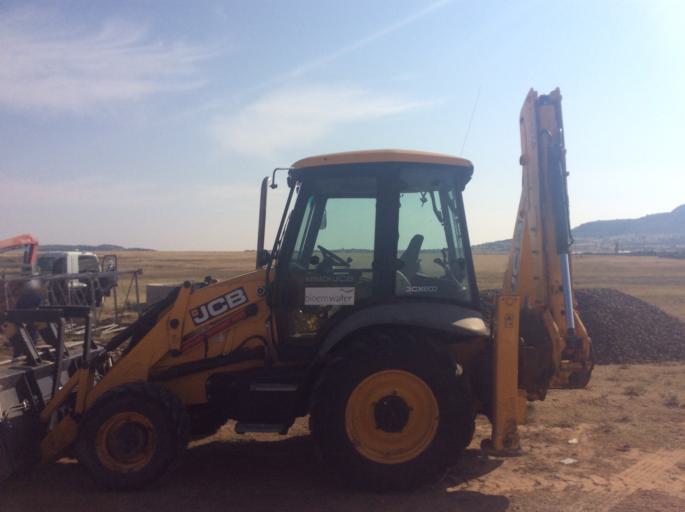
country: LS
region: Mafeteng
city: Mafeteng
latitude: -29.7143
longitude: 27.0086
